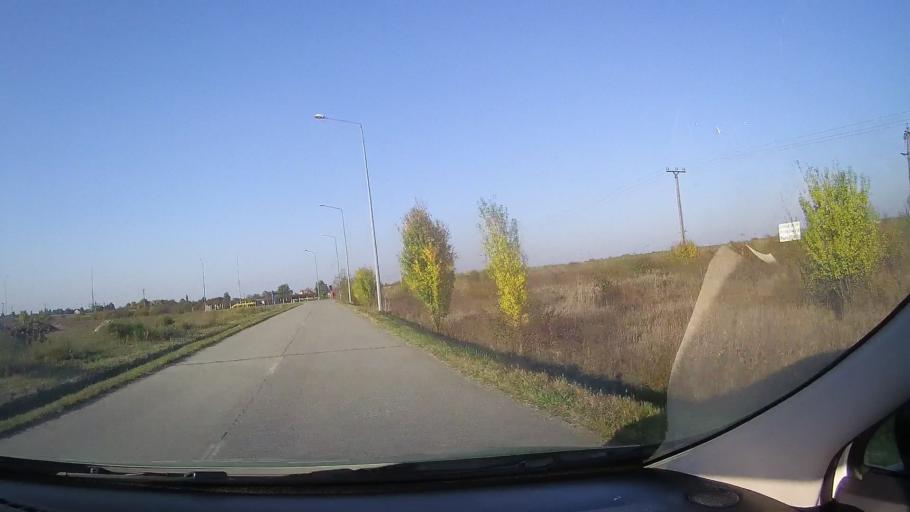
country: RO
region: Bihor
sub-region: Comuna Bors
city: Santion
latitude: 47.1089
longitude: 21.8316
